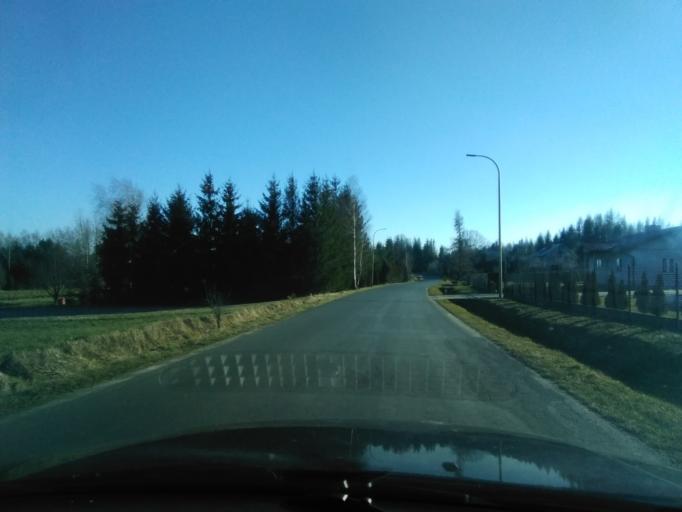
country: PL
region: Subcarpathian Voivodeship
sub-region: Powiat krosnienski
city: Rymanow
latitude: 49.5656
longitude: 21.8892
